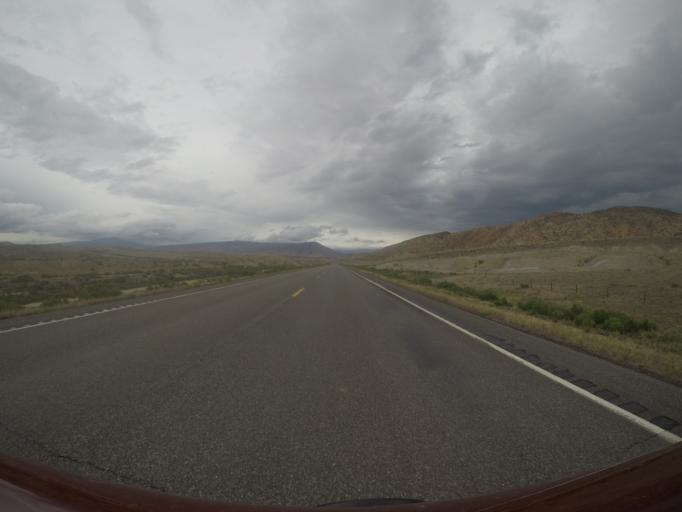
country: US
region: Wyoming
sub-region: Big Horn County
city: Lovell
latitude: 44.9324
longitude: -108.2980
